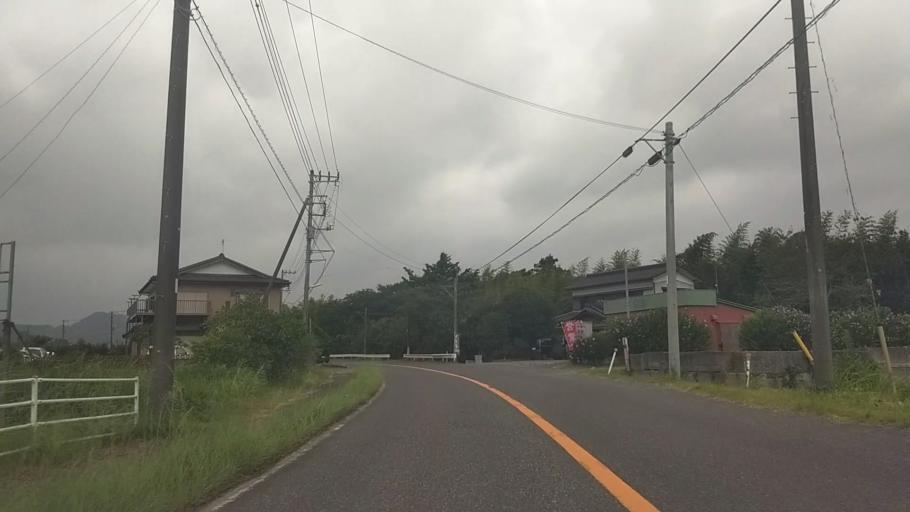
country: JP
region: Chiba
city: Kawaguchi
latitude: 35.1370
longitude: 139.9967
